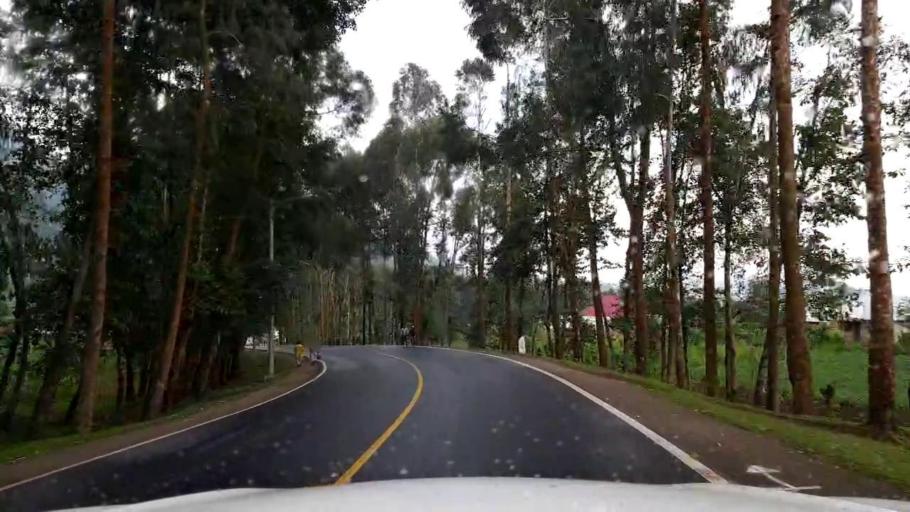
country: RW
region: Western Province
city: Gisenyi
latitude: -1.6694
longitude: 29.3620
